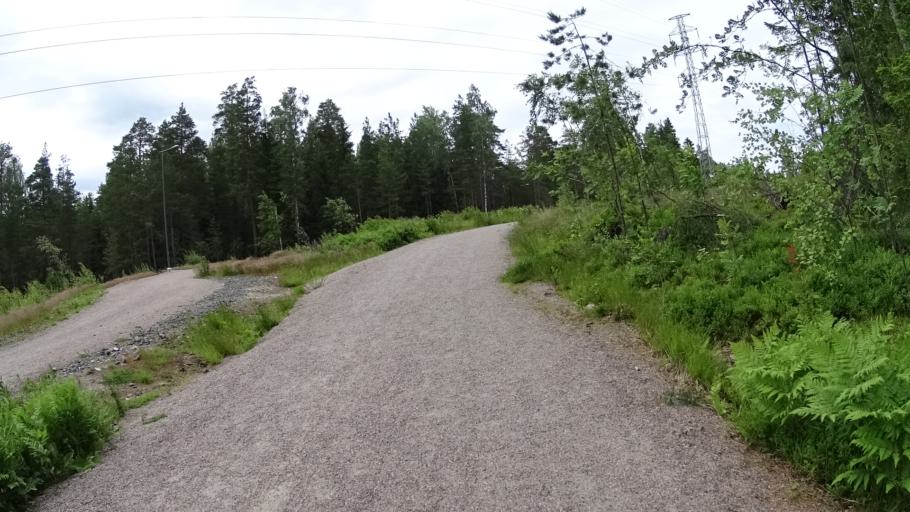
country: FI
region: Uusimaa
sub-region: Helsinki
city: Kauniainen
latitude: 60.1830
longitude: 24.7182
